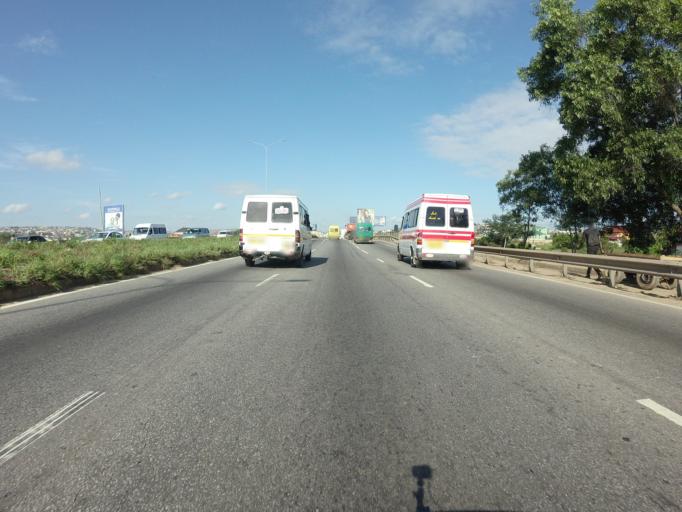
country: GH
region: Greater Accra
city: Gbawe
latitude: 5.5536
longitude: -0.3123
